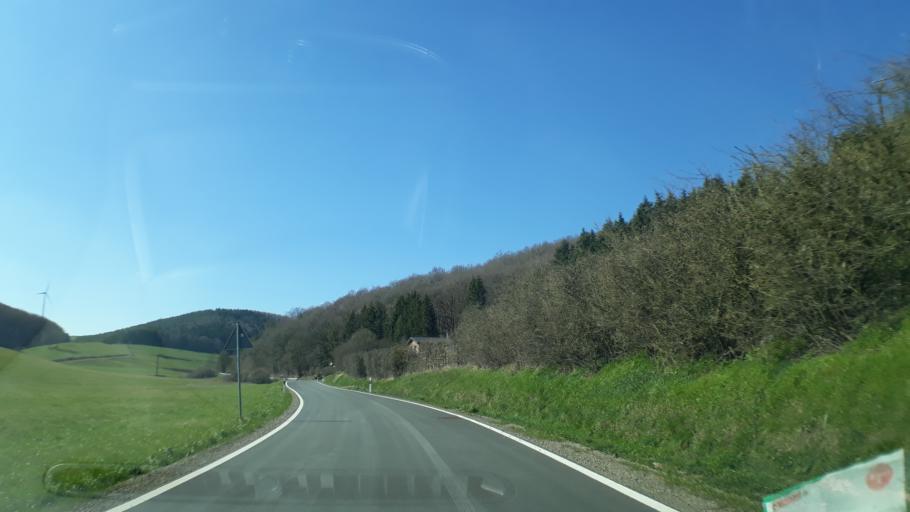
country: DE
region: North Rhine-Westphalia
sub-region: Regierungsbezirk Koln
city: Mechernich
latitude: 50.5485
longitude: 6.6395
